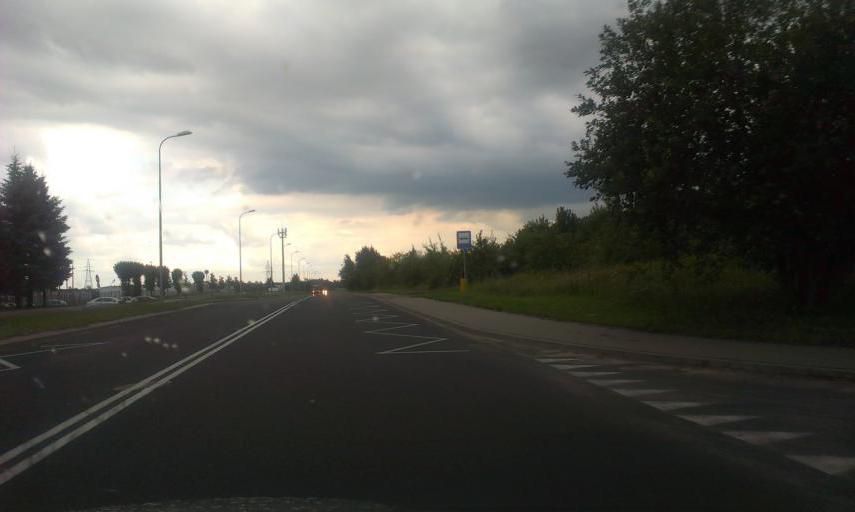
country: PL
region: West Pomeranian Voivodeship
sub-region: Koszalin
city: Koszalin
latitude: 54.1927
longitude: 16.1463
